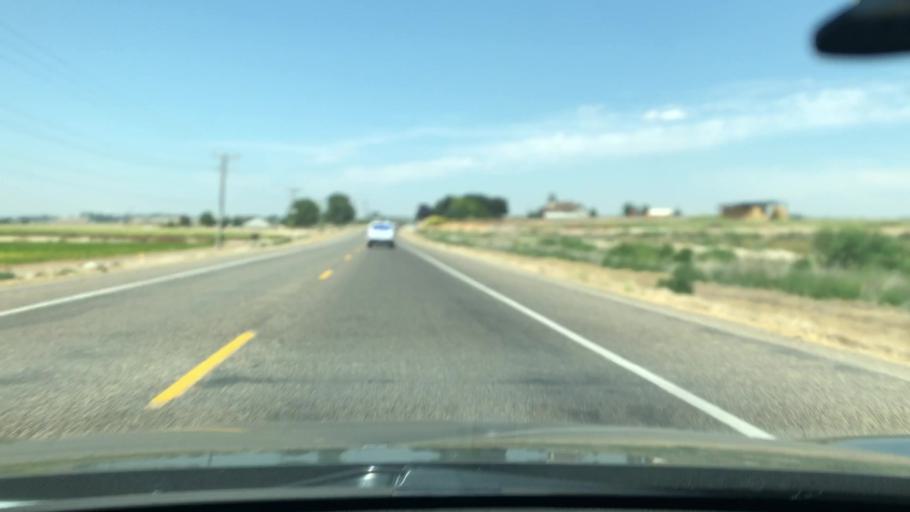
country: US
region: Idaho
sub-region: Owyhee County
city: Homedale
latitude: 43.6354
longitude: -116.9116
